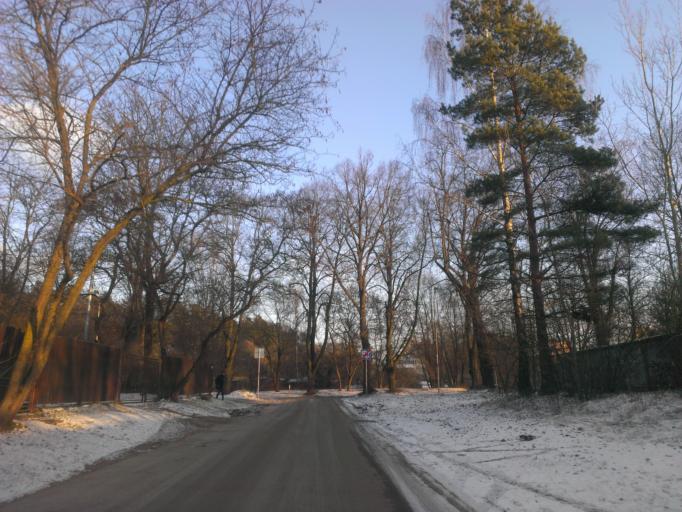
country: LV
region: Riga
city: Jaunciems
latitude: 56.9960
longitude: 24.1615
